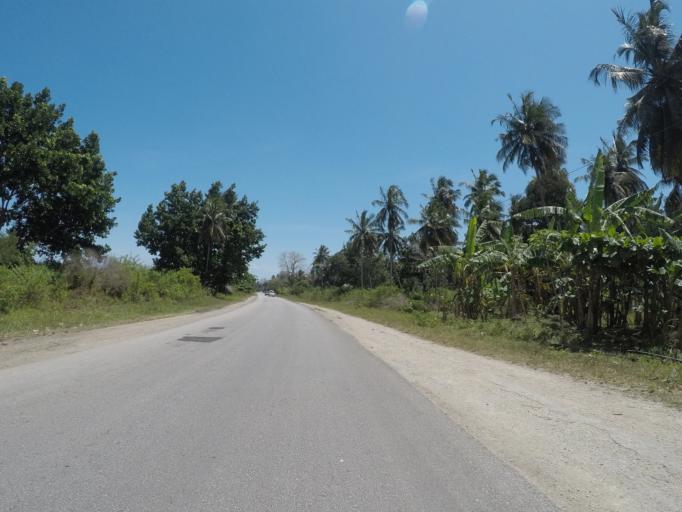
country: TZ
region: Zanzibar Central/South
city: Nganane
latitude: -6.2698
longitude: 39.4262
